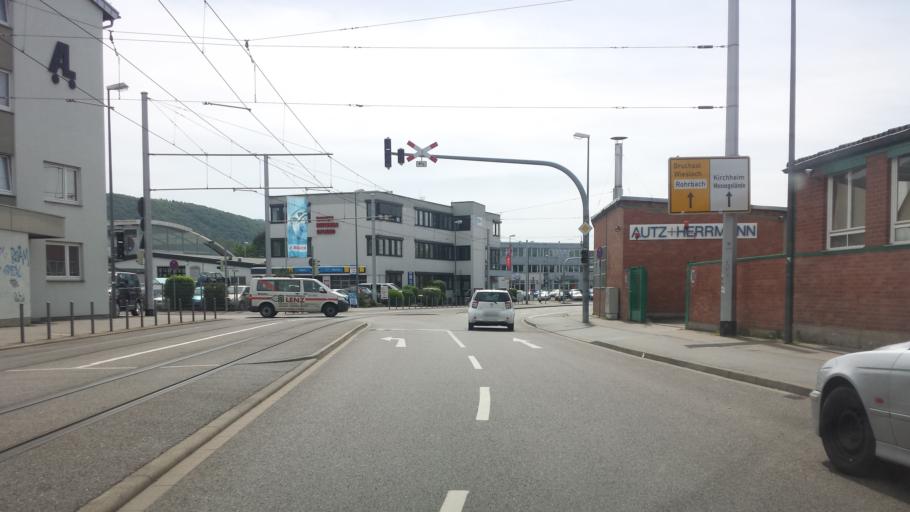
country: DE
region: Baden-Wuerttemberg
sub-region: Karlsruhe Region
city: Heidelberg
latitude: 49.3982
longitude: 8.6791
